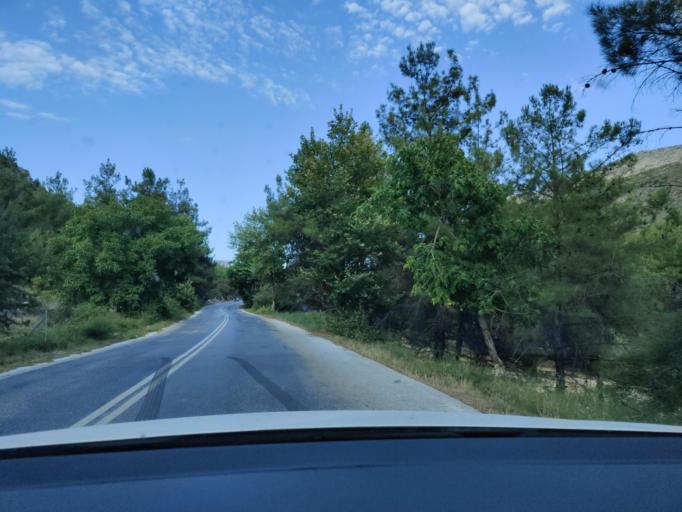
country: GR
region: East Macedonia and Thrace
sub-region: Nomos Kavalas
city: Limenaria
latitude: 40.6174
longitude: 24.6477
